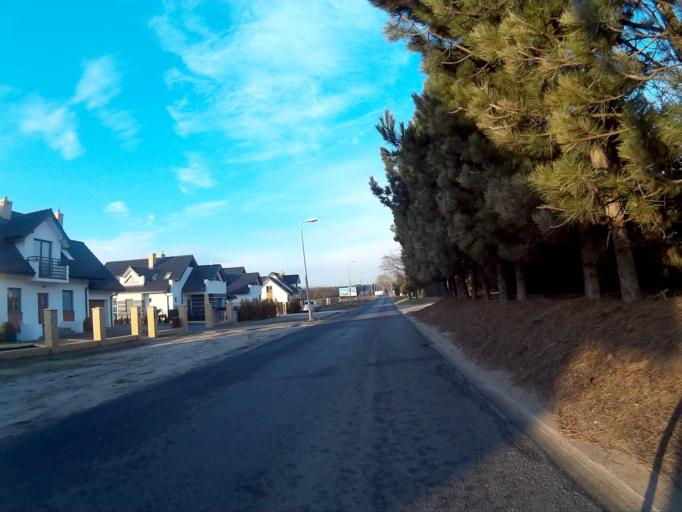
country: PL
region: Kujawsko-Pomorskie
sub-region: Powiat bydgoski
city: Osielsko
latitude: 53.1603
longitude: 18.0814
